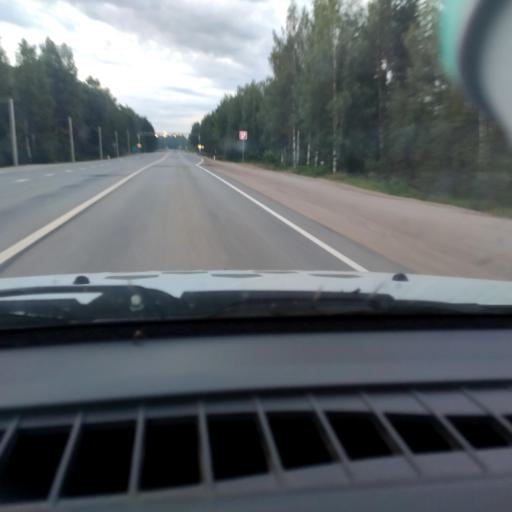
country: RU
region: Kirov
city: Murygino
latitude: 58.7209
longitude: 49.5791
